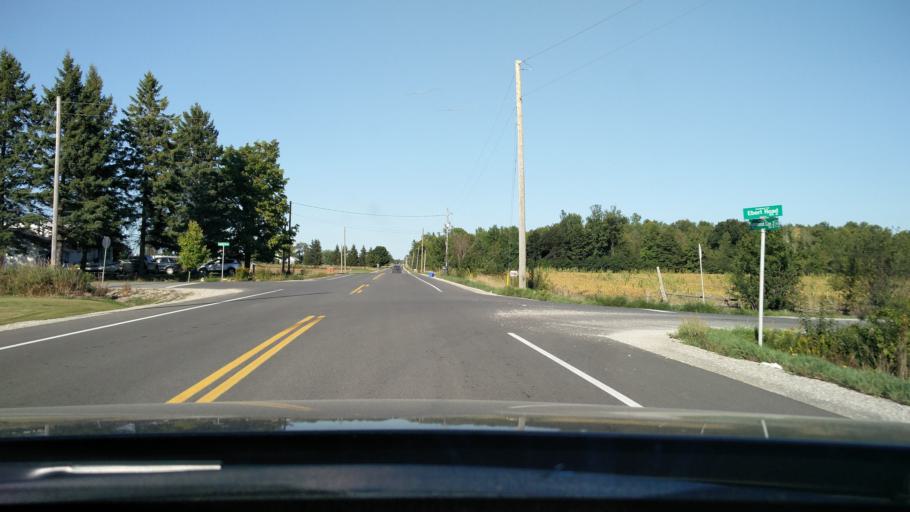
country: CA
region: Ontario
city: Perth
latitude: 44.9323
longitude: -76.2019
